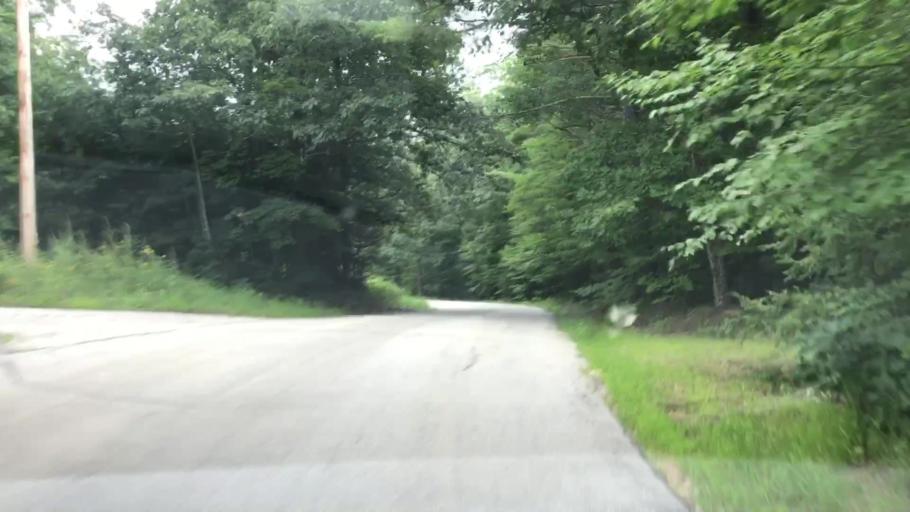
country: US
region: New Hampshire
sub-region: Hillsborough County
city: Milford
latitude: 42.8759
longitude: -71.6187
